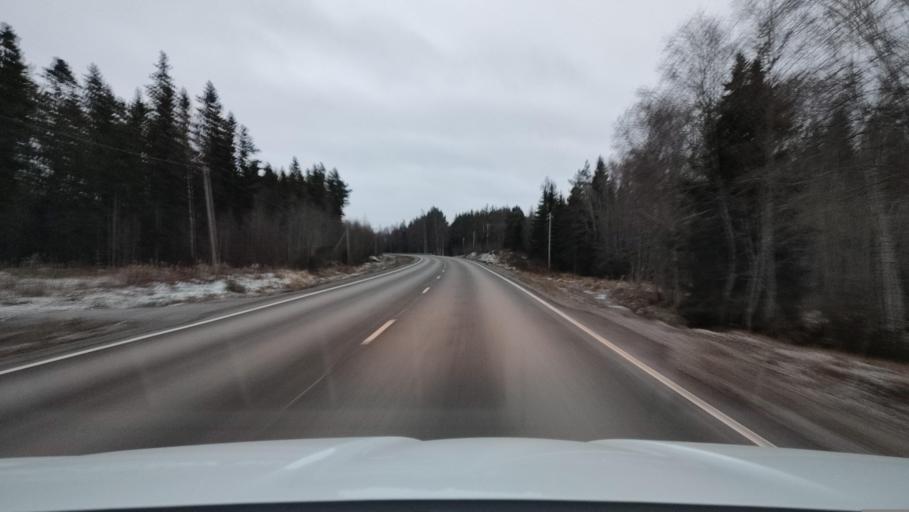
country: FI
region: Ostrobothnia
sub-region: Vaasa
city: Replot
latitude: 63.2121
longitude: 21.4311
